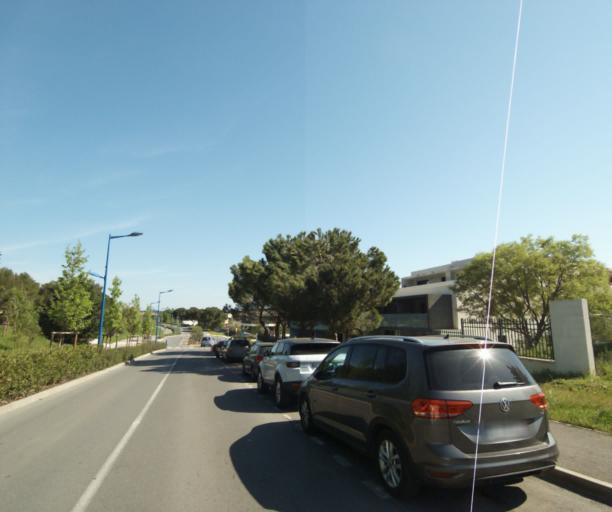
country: FR
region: Languedoc-Roussillon
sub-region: Departement de l'Herault
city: Le Cres
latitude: 43.6530
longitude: 3.9349
